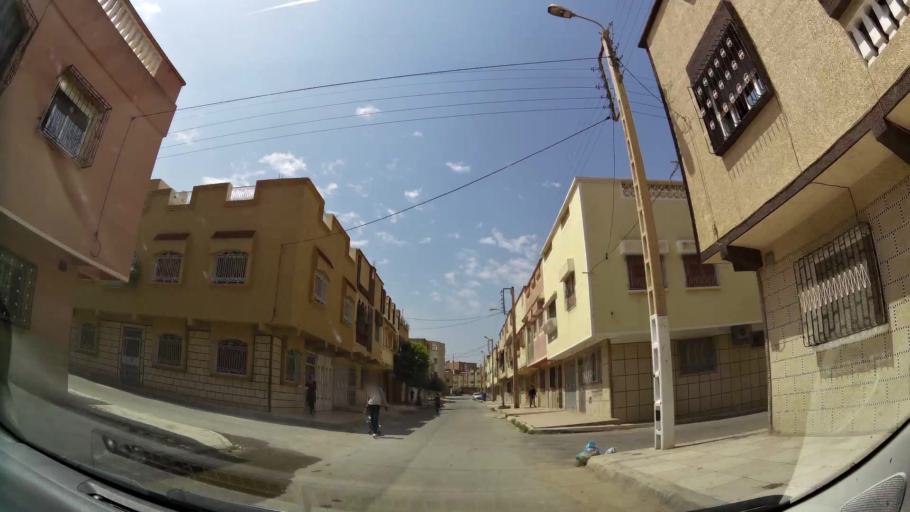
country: MA
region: Oriental
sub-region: Oujda-Angad
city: Oujda
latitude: 34.6842
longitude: -1.8842
